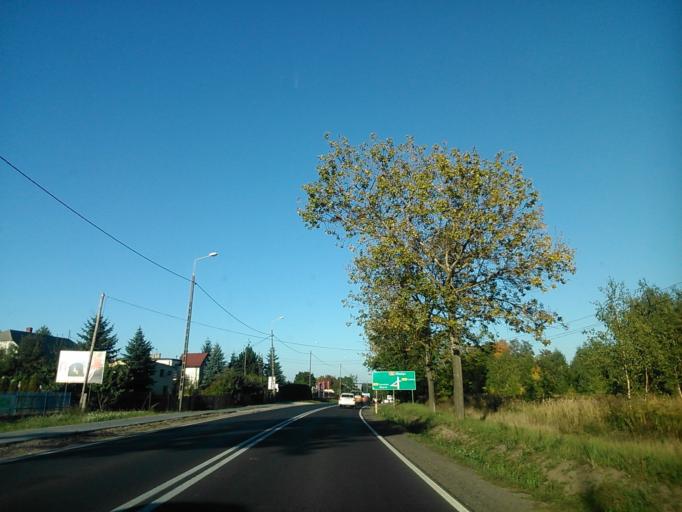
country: PL
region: Kujawsko-Pomorskie
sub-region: Powiat torunski
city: Lubicz Dolny
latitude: 53.0548
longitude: 18.7126
